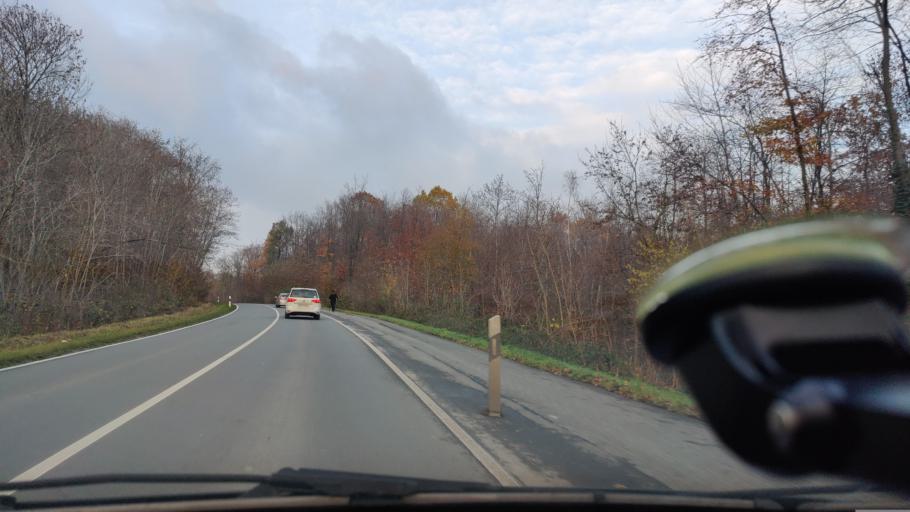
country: DE
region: North Rhine-Westphalia
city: Lunen
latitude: 51.6436
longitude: 7.5325
